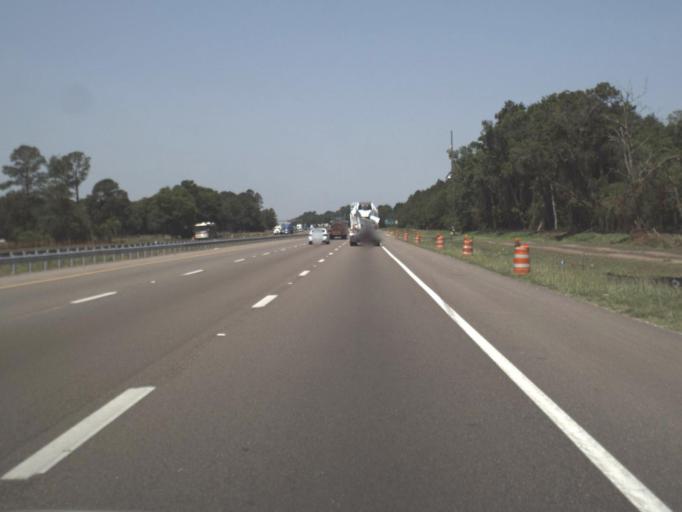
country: US
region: Florida
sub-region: Duval County
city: Jacksonville
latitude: 30.3150
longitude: -81.7941
